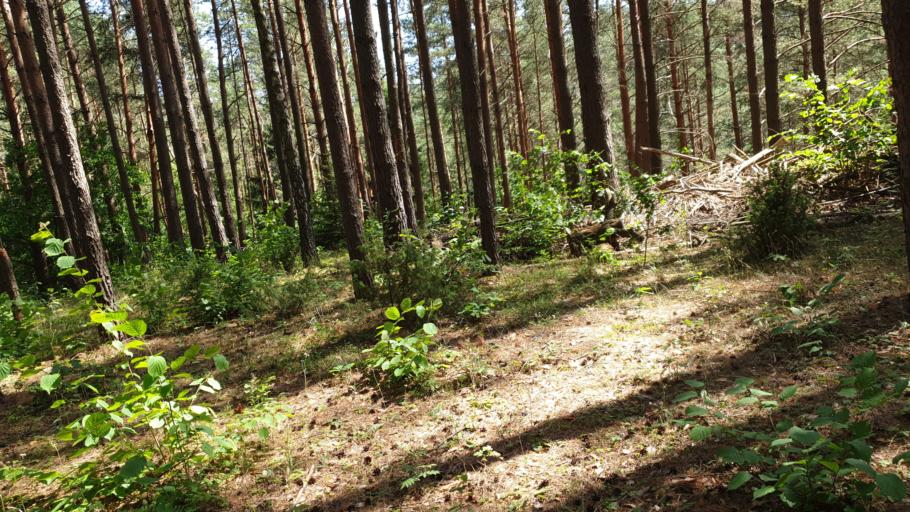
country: LT
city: Grigiskes
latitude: 54.7827
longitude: 24.9905
